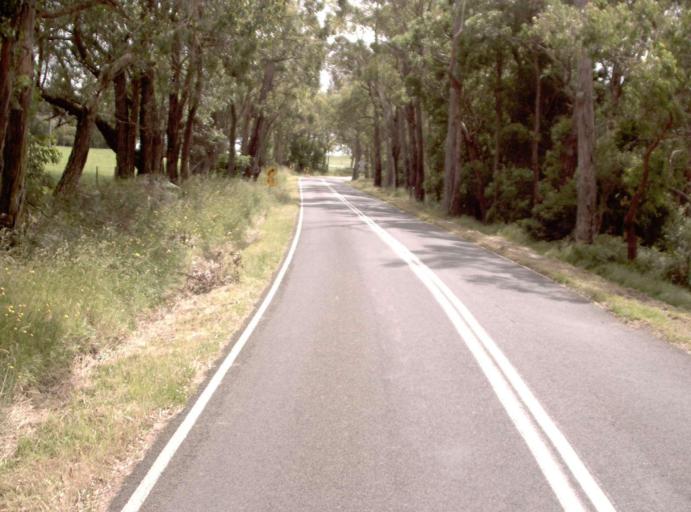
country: AU
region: Victoria
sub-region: Latrobe
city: Moe
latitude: -38.0763
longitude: 146.1703
